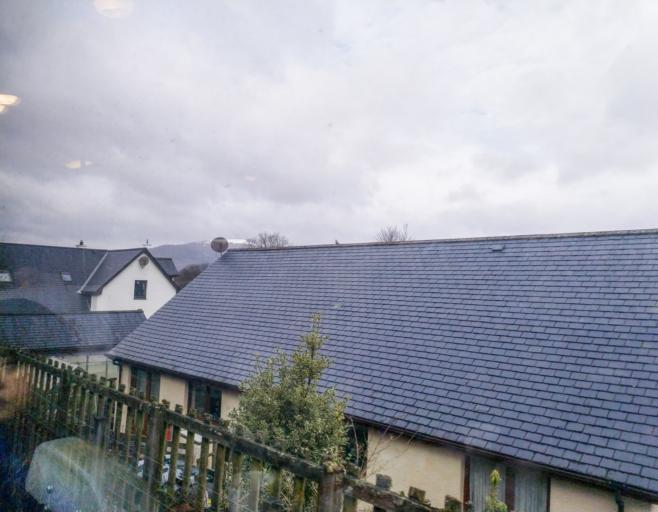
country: GB
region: Scotland
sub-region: Highland
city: Spean Bridge
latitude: 56.8895
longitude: -4.9265
